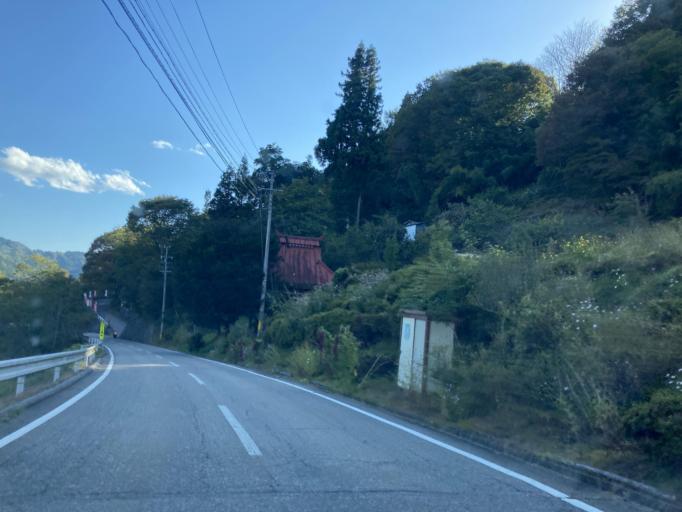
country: JP
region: Nagano
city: Omachi
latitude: 36.4916
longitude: 137.9120
